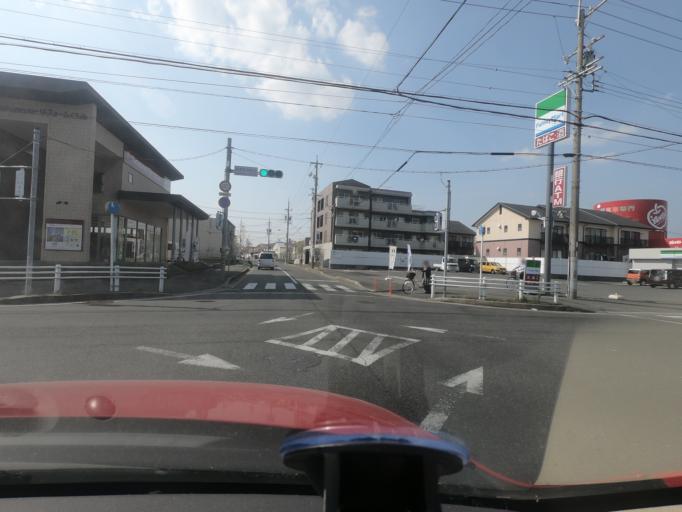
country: JP
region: Aichi
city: Kasugai
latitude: 35.2502
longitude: 136.9672
